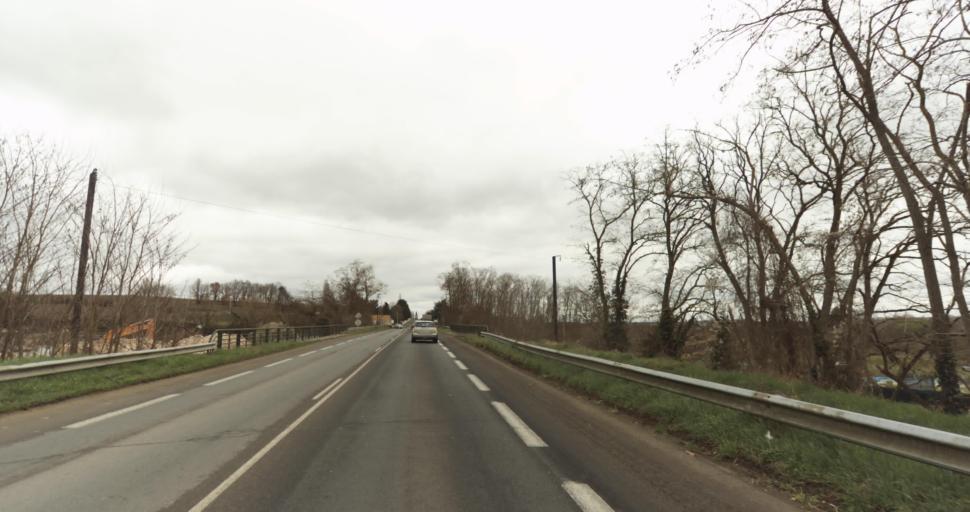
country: FR
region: Pays de la Loire
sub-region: Departement de Maine-et-Loire
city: Varrains
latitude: 47.2344
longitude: -0.0750
